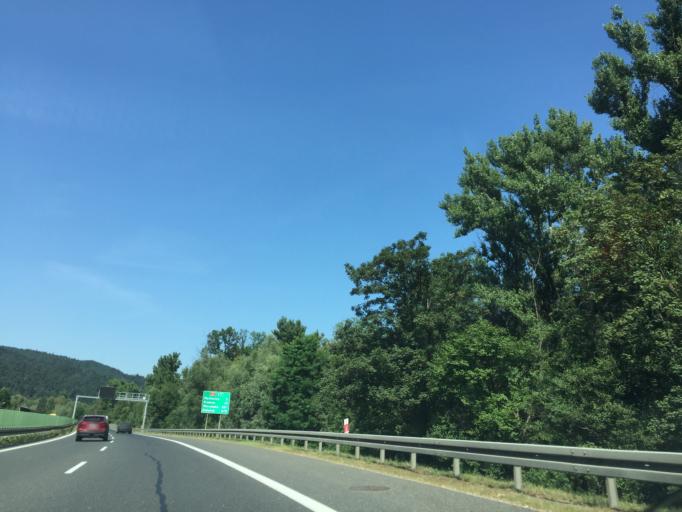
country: PL
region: Lesser Poland Voivodeship
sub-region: Powiat myslenicki
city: Stroza
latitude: 49.8033
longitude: 19.9255
